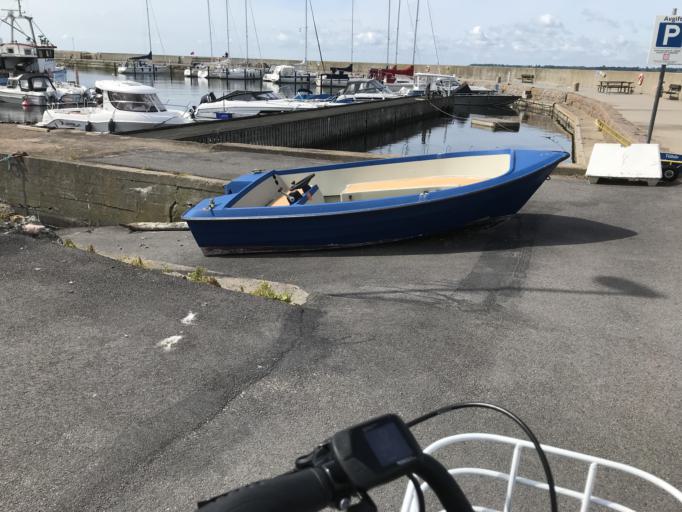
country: SE
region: Skane
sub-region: Helsingborg
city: Rydeback
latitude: 55.9404
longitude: 12.7722
